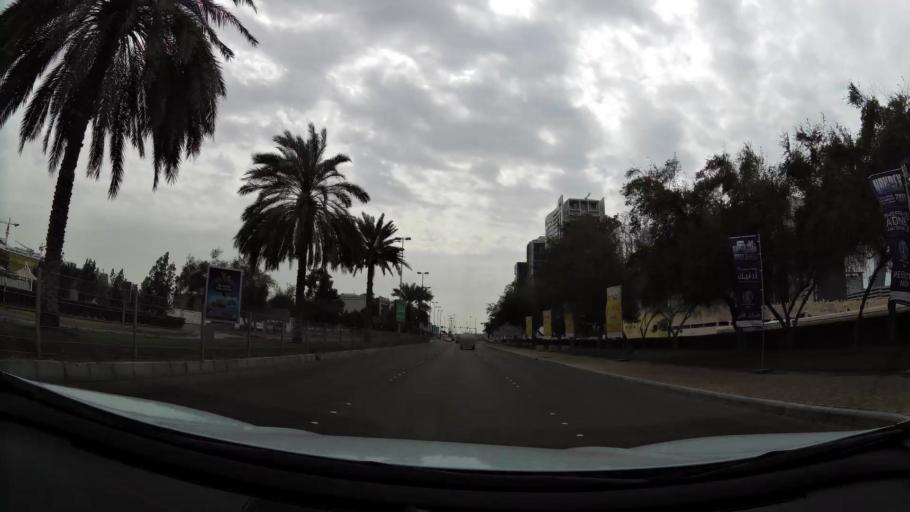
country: AE
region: Abu Dhabi
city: Abu Dhabi
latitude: 24.4229
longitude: 54.4446
